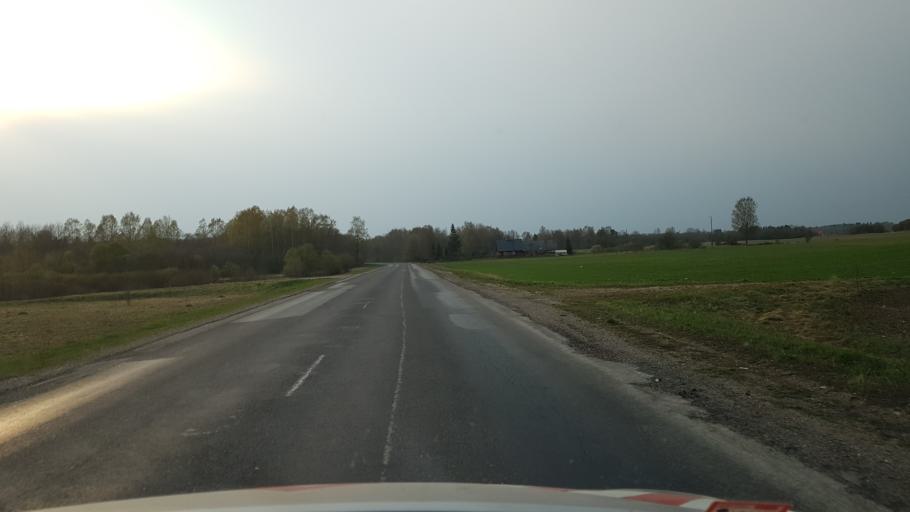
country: EE
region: Harju
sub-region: Raasiku vald
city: Raasiku
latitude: 59.3412
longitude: 25.1371
